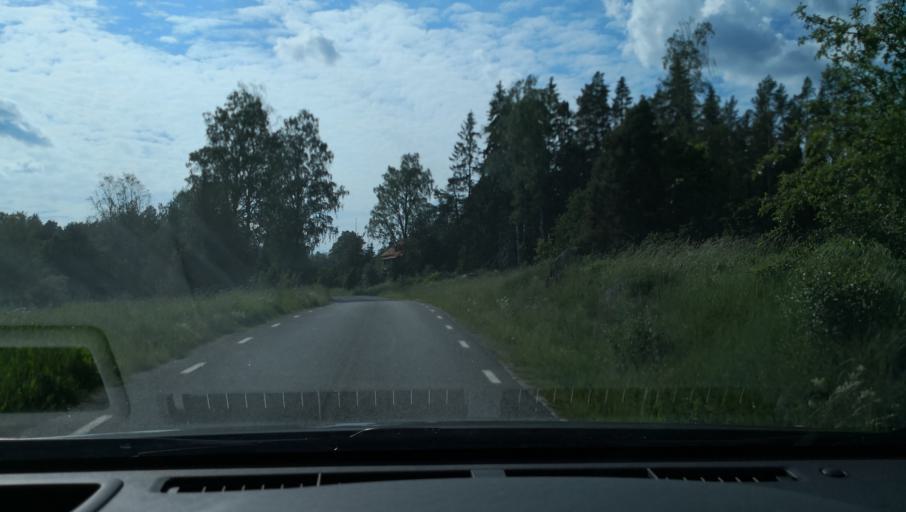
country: SE
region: Uppsala
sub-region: Enkopings Kommun
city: Orsundsbro
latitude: 59.8420
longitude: 17.1919
